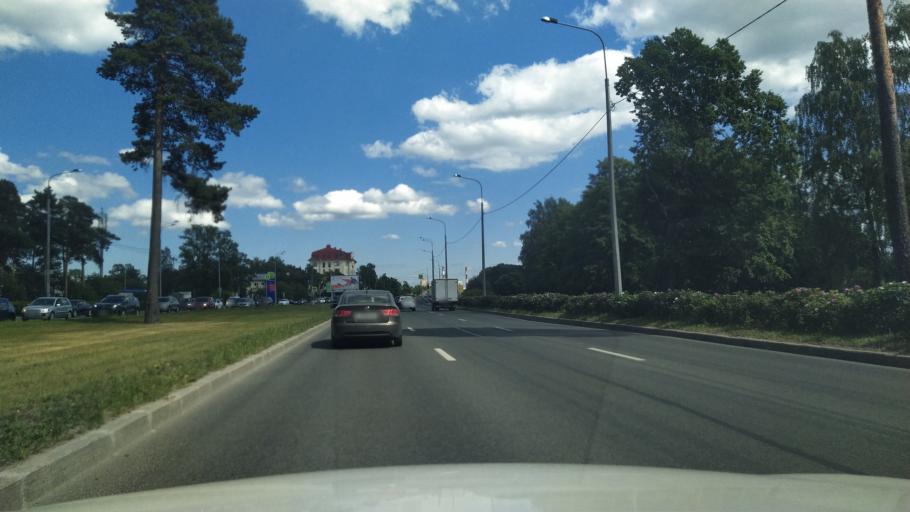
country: RU
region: Leningrad
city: Kalininskiy
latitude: 59.9948
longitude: 30.4038
